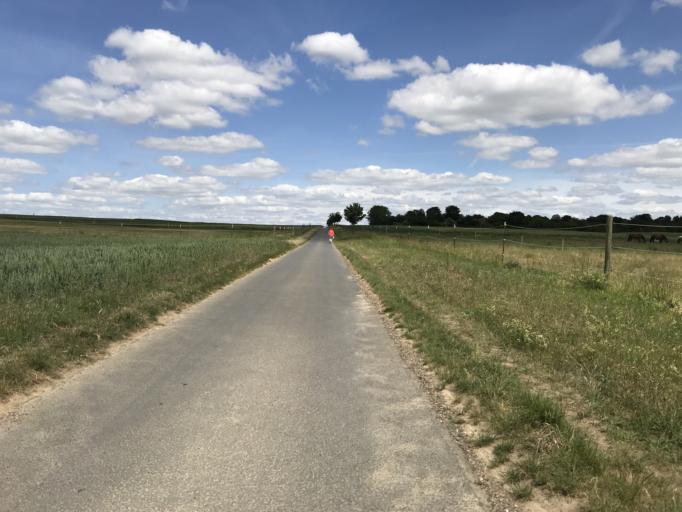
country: DE
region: Hesse
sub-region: Regierungsbezirk Darmstadt
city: Ober-Morlen
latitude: 50.3800
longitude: 8.6952
